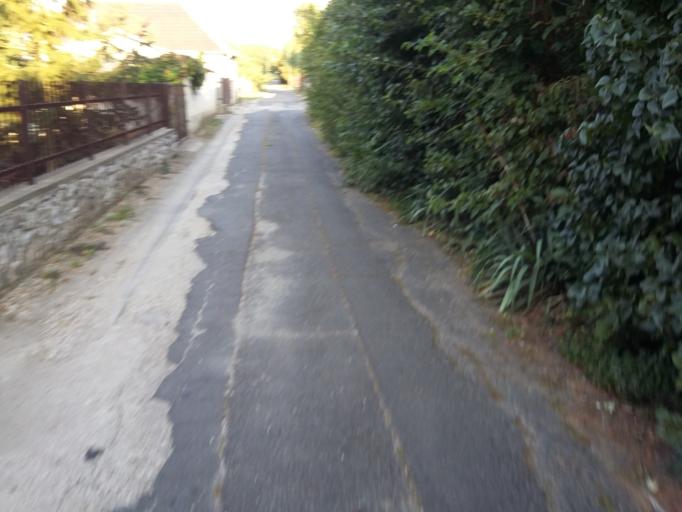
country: HU
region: Borsod-Abauj-Zemplen
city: Bekecs
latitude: 48.1581
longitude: 21.1824
